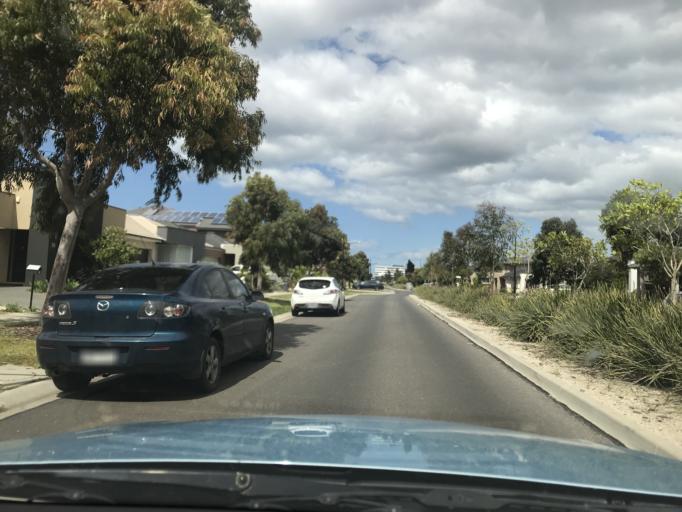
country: AU
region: Victoria
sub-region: Wyndham
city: Williams Landing
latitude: -37.8605
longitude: 144.7433
